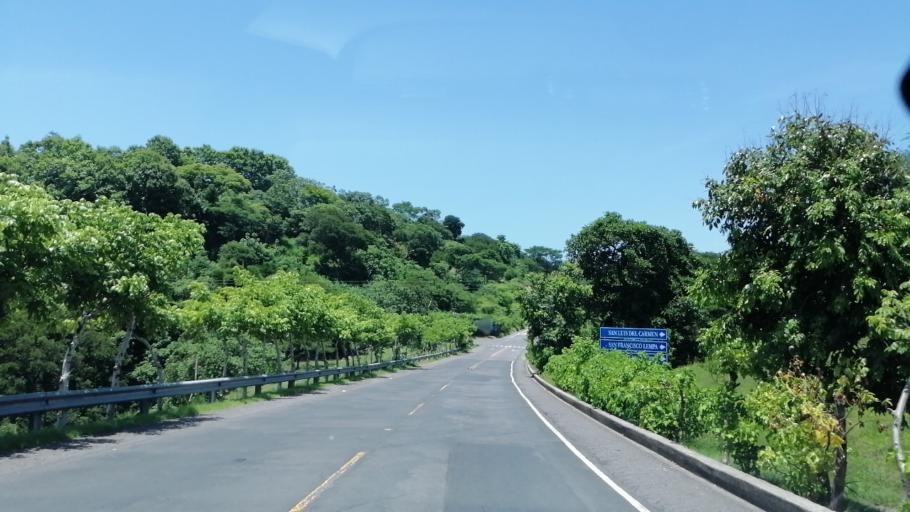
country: SV
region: Chalatenango
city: Chalatenango
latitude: 14.0290
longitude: -88.9405
